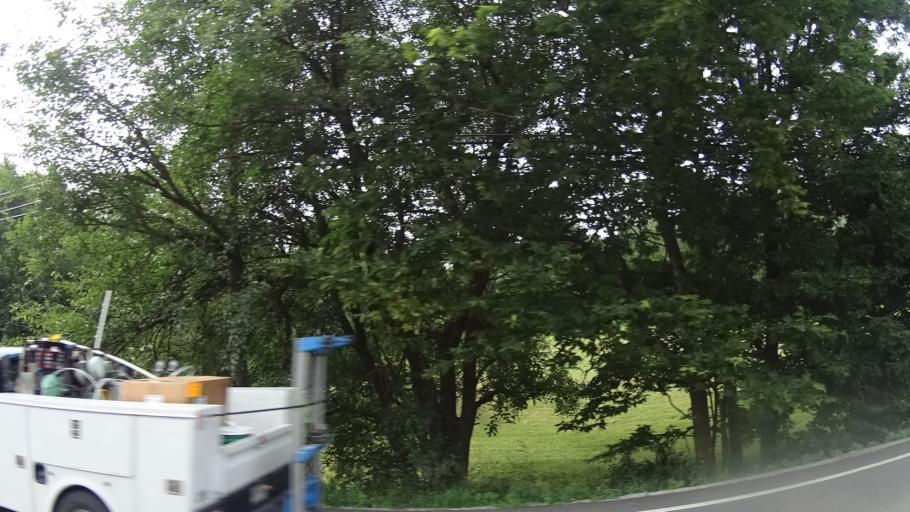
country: US
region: Indiana
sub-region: Madison County
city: Pendleton
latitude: 40.0034
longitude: -85.7611
